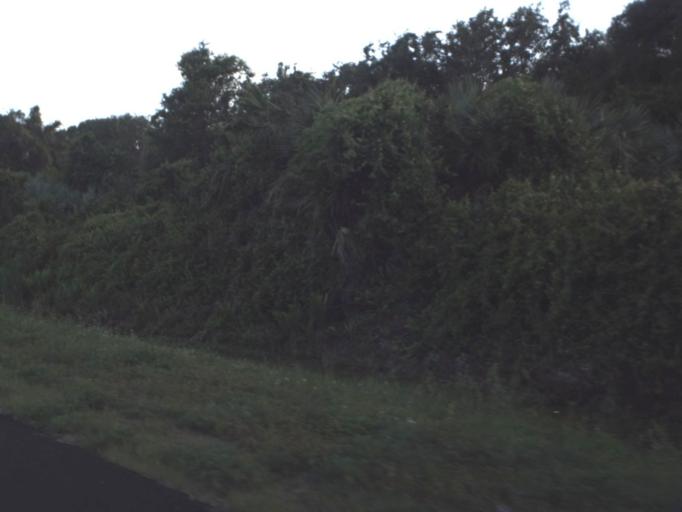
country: US
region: Florida
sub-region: Brevard County
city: South Patrick Shores
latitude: 28.2434
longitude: -80.6788
